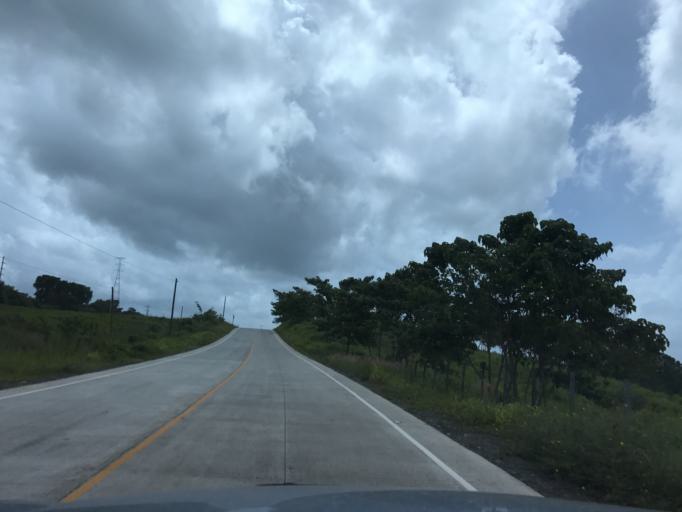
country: GT
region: Izabal
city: El Estor
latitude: 15.6169
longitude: -89.0734
